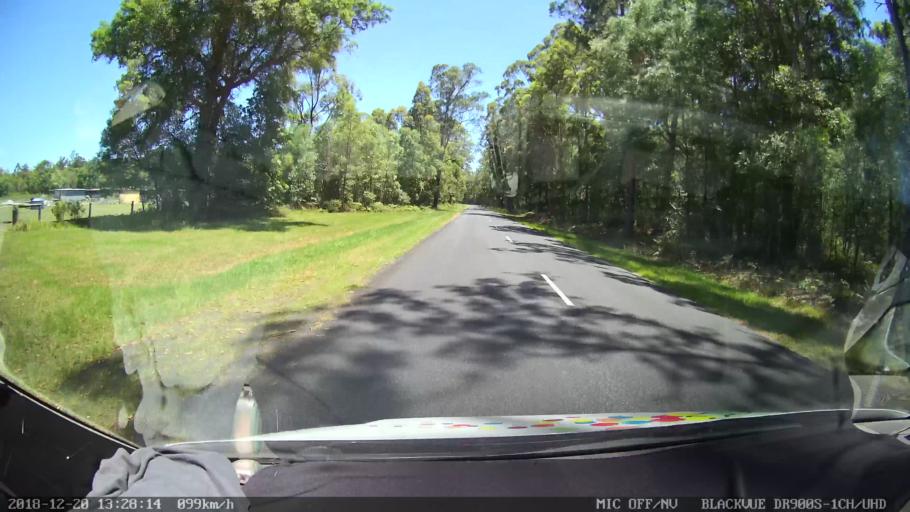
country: AU
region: New South Wales
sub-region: Clarence Valley
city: Gordon
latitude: -29.1718
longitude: 152.9912
